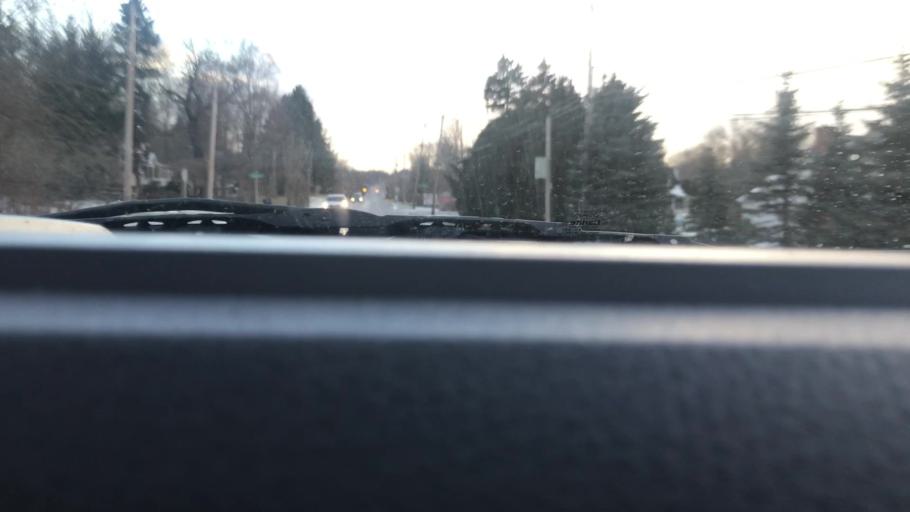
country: US
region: Ohio
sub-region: Mahoning County
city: Canfield
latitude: 41.0385
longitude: -80.7607
